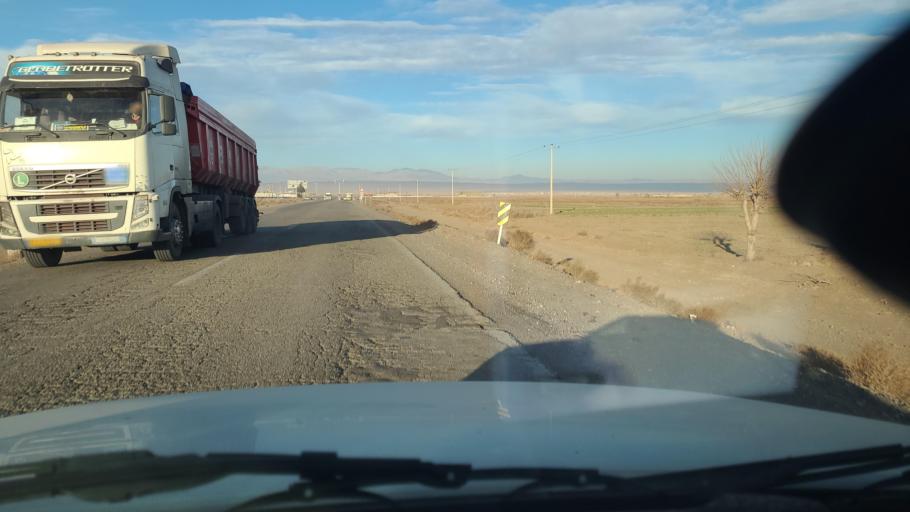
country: IR
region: Razavi Khorasan
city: Neqab
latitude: 36.5815
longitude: 57.5797
